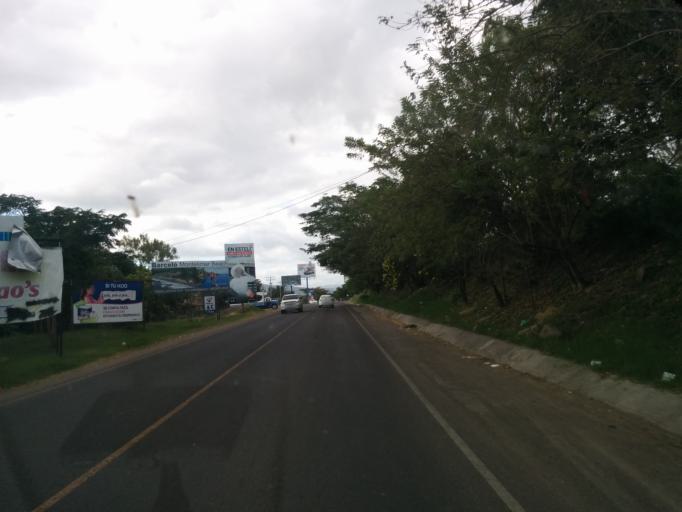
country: NI
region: Esteli
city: Esteli
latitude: 13.0622
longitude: -86.3457
